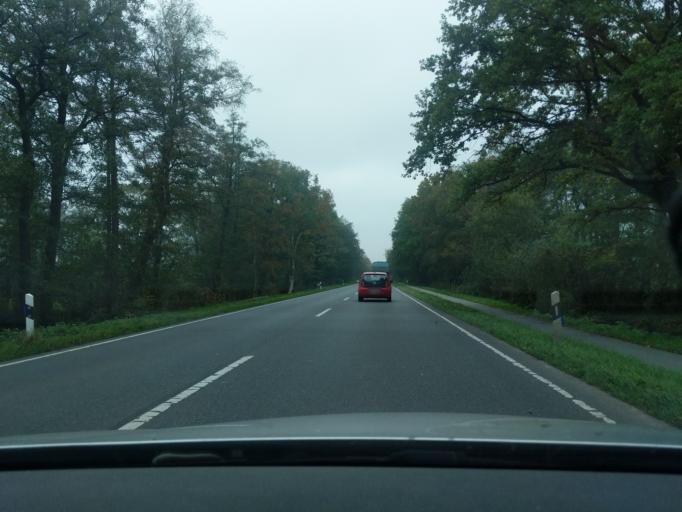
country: DE
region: Lower Saxony
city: Burweg
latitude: 53.6286
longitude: 9.2615
